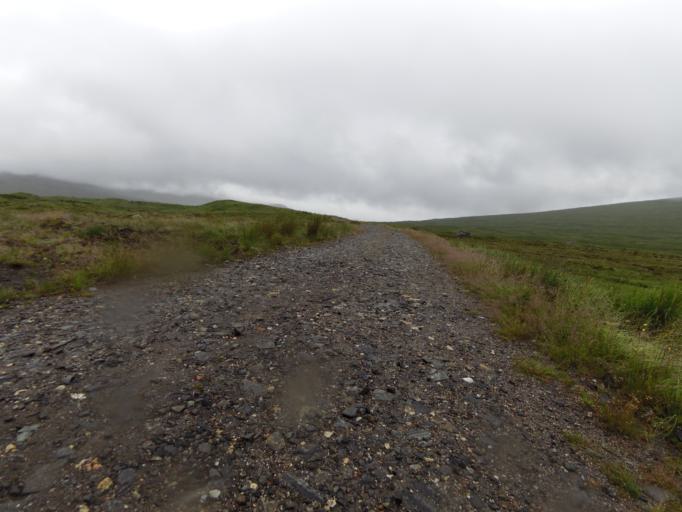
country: GB
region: Scotland
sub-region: Highland
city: Spean Bridge
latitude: 56.7654
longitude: -4.6675
